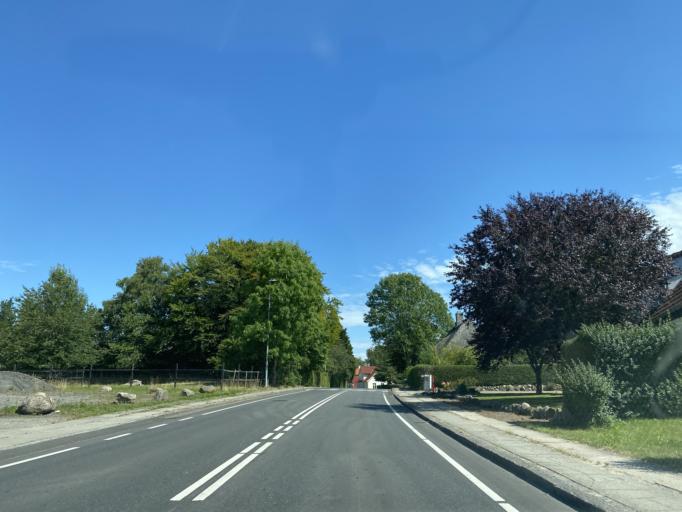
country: DK
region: South Denmark
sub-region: Faaborg-Midtfyn Kommune
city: Ringe
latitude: 55.2436
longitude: 10.5400
